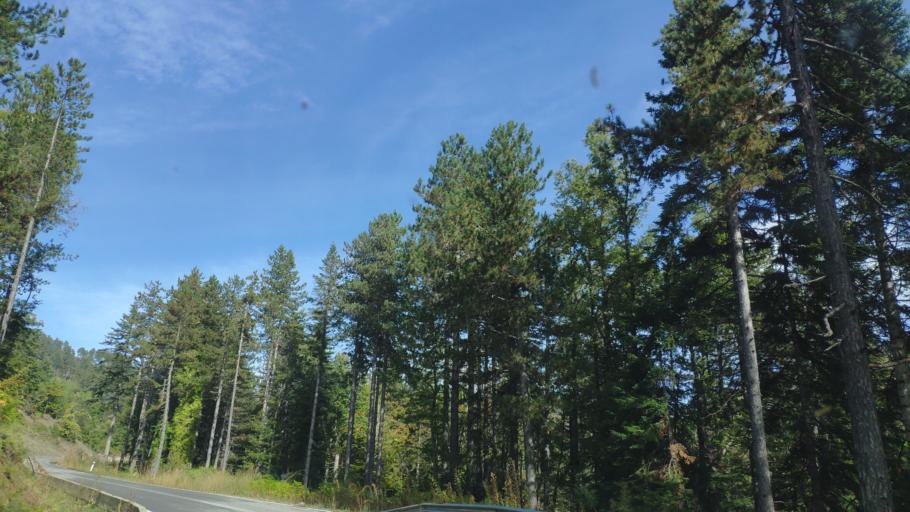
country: AL
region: Korce
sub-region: Rrethi i Devollit
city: Miras
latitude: 40.3857
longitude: 20.9131
